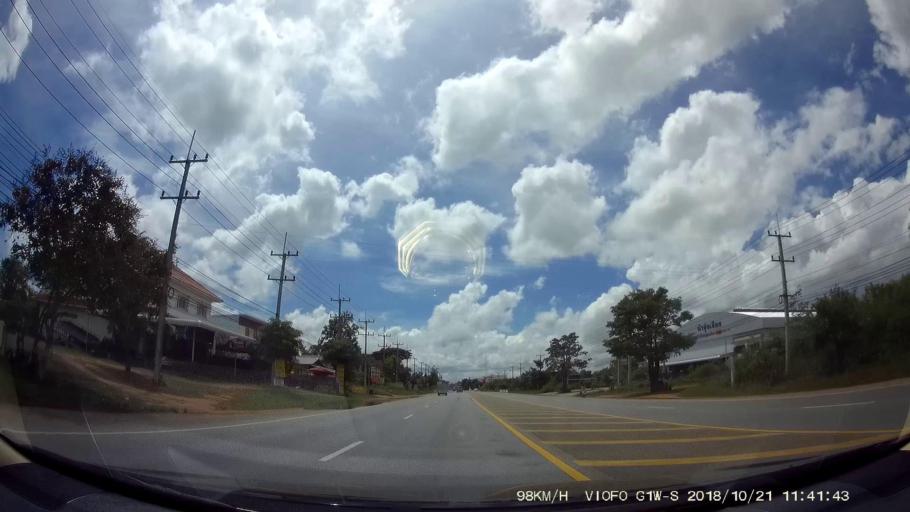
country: TH
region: Chaiyaphum
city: Chaiyaphum
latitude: 15.6951
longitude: 102.0133
